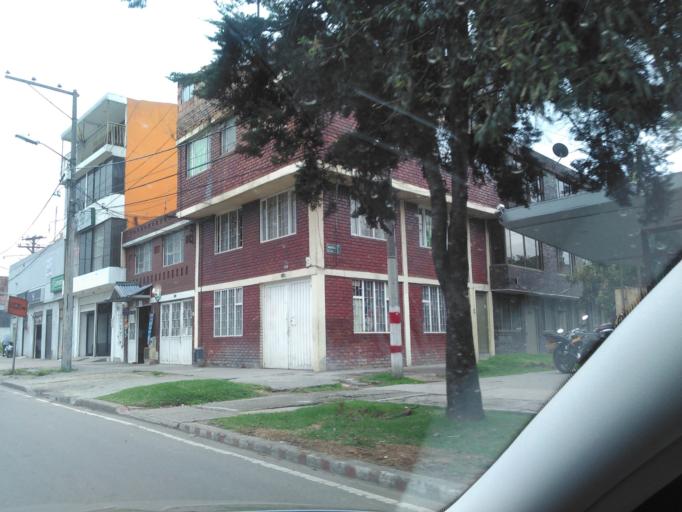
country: CO
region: Bogota D.C.
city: Bogota
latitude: 4.6191
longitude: -74.1061
